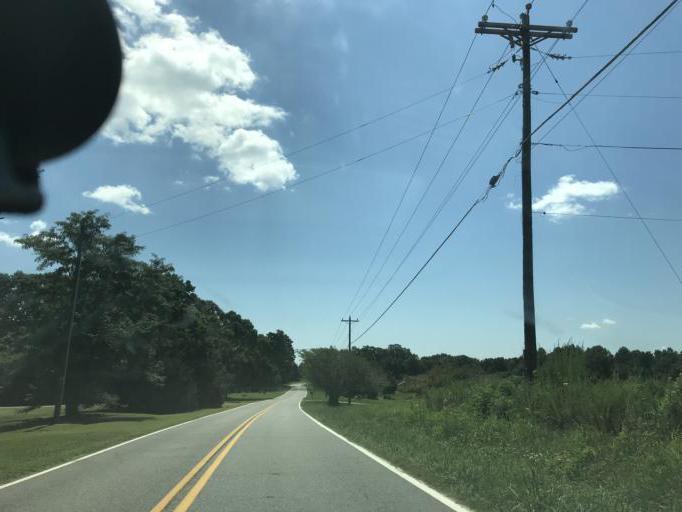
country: US
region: Georgia
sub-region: Forsyth County
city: Cumming
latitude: 34.2964
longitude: -84.0283
